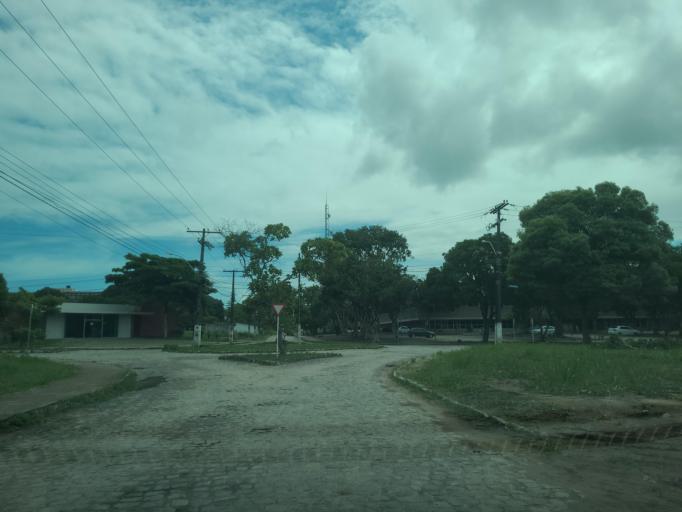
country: BR
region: Alagoas
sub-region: Satuba
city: Satuba
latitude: -9.5568
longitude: -35.7771
